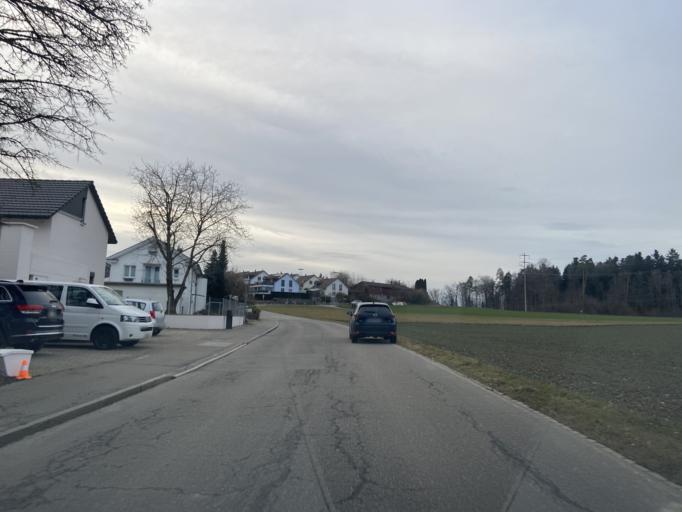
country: CH
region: Zurich
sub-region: Bezirk Winterthur
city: Brutten
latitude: 47.4754
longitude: 8.6813
